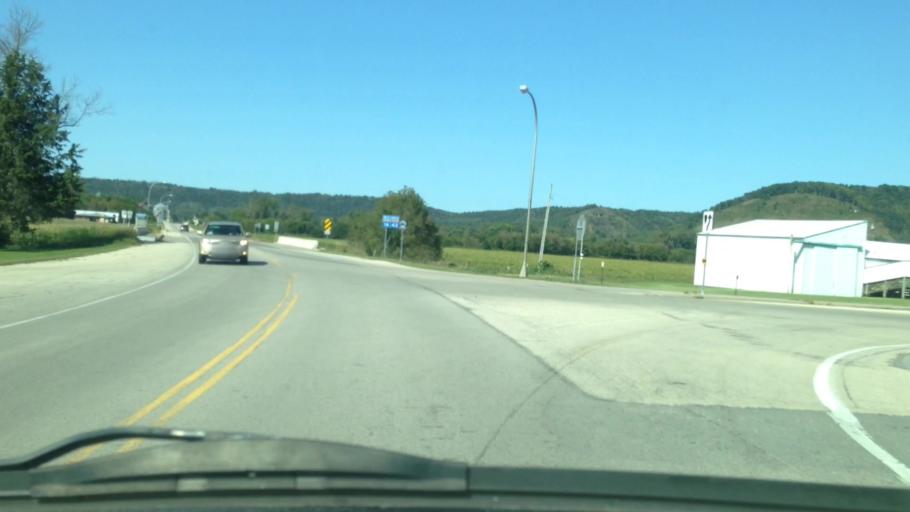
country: US
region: Minnesota
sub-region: Fillmore County
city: Rushford
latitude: 43.7974
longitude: -91.7530
